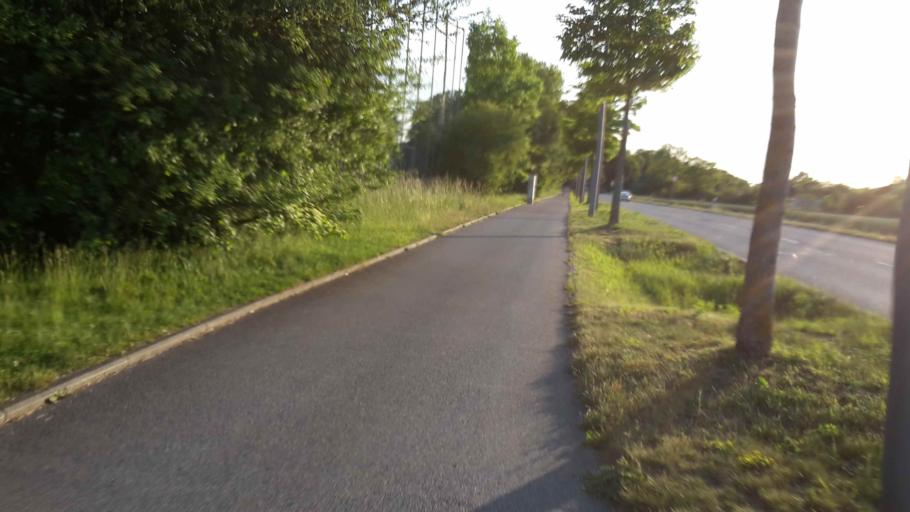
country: DE
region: Bavaria
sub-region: Upper Bavaria
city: Karlsfeld
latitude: 48.2174
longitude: 11.4936
